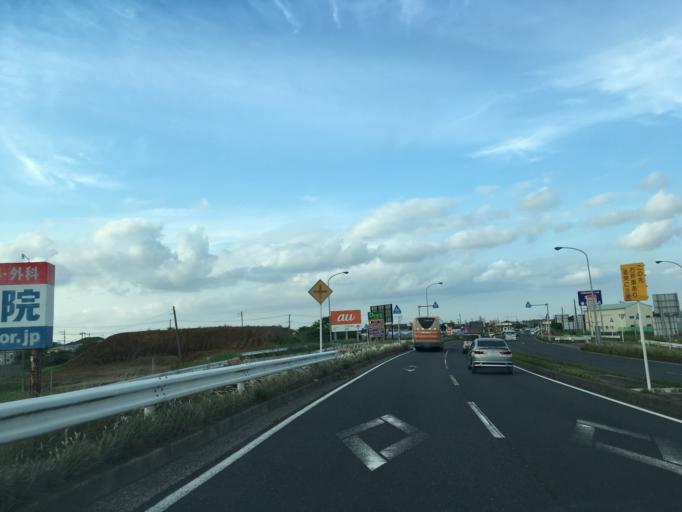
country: JP
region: Chiba
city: Kisarazu
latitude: 35.4037
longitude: 139.9424
